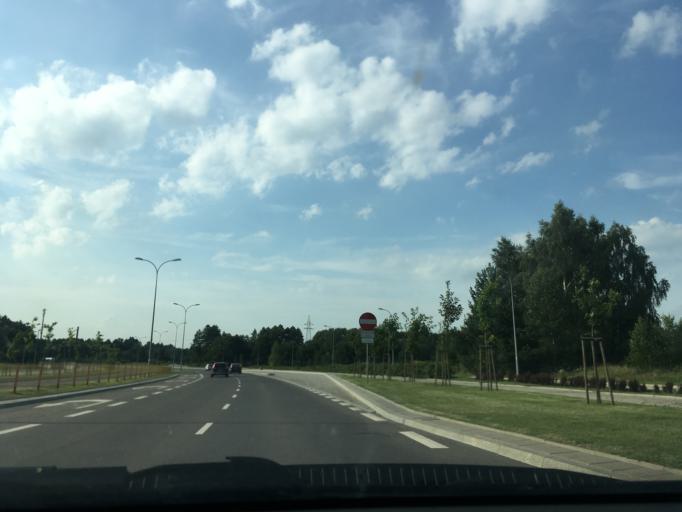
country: PL
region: Podlasie
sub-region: Bialystok
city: Bialystok
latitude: 53.1361
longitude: 23.2208
